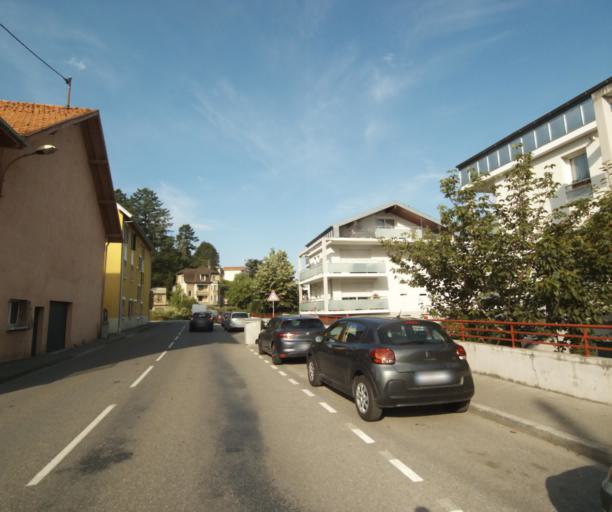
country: FR
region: Rhone-Alpes
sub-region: Departement de la Haute-Savoie
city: Thonon-les-Bains
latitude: 46.3711
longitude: 6.4919
